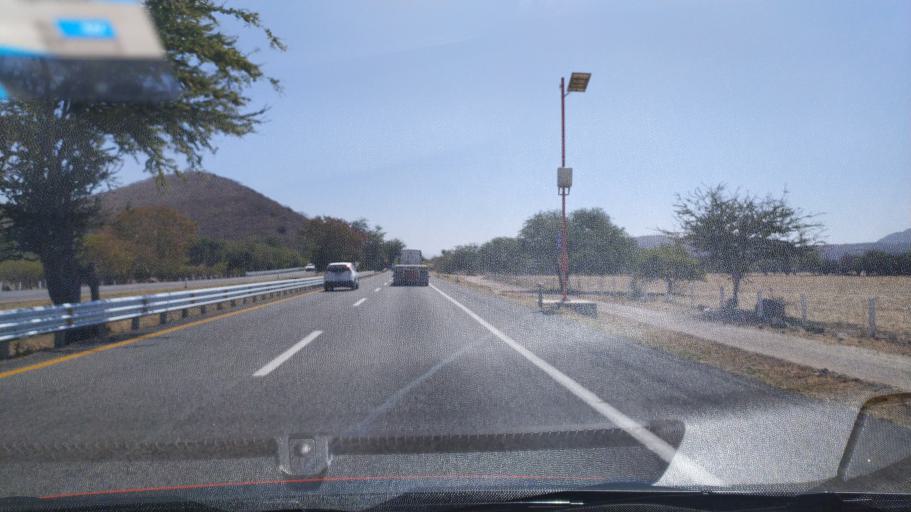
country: MX
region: Jalisco
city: Zacoalco de Torres
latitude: 20.2012
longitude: -103.5256
